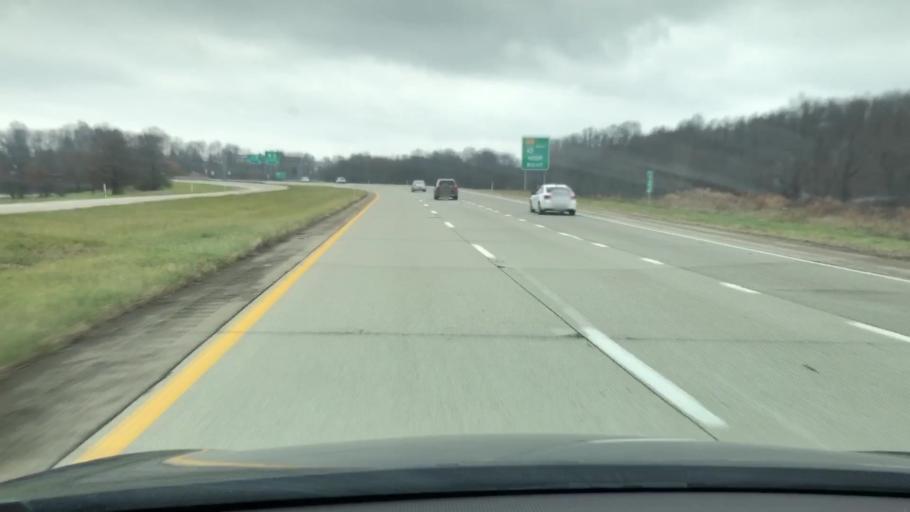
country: US
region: Pennsylvania
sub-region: Fayette County
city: Leith-Hatfield
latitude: 39.8756
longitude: -79.7453
